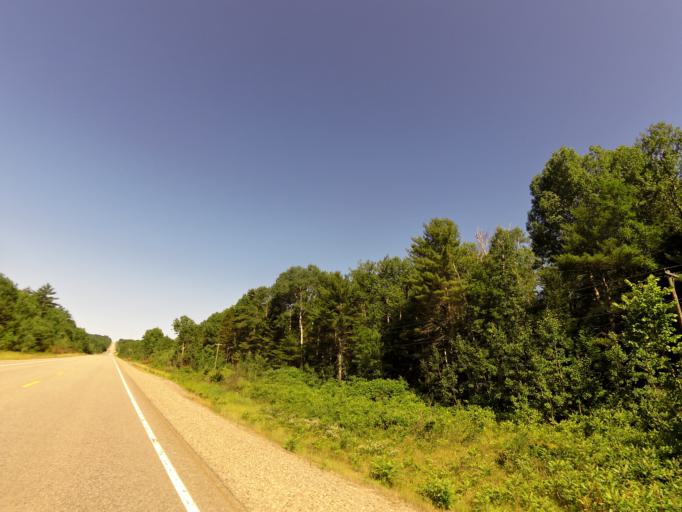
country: CA
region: Ontario
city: Deep River
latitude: 46.2124
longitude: -77.9176
